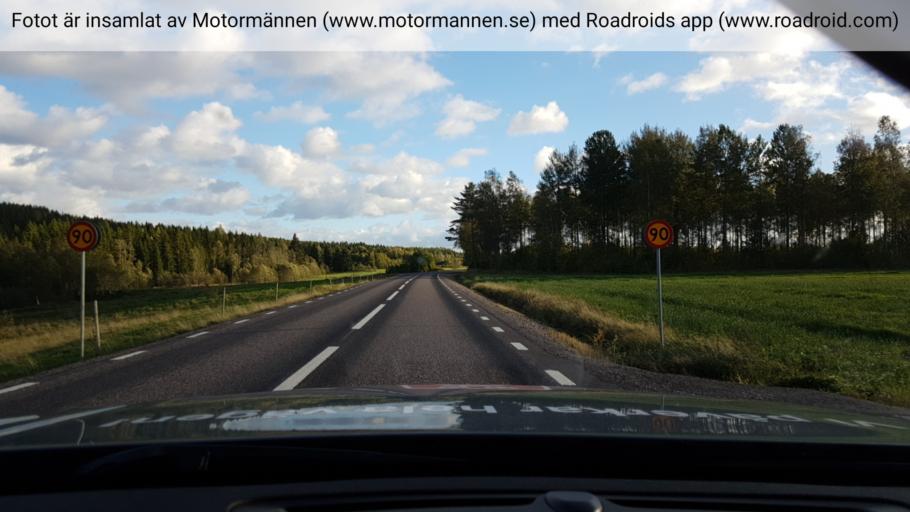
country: SE
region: Vaermland
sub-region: Karlstads Kommun
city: Molkom
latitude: 59.7103
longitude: 13.6794
